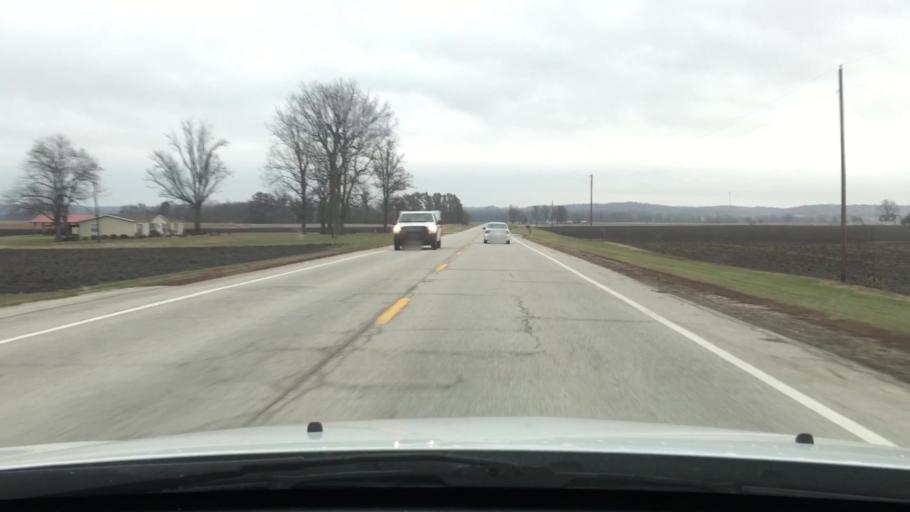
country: US
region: Missouri
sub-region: Pike County
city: Louisiana
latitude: 39.4889
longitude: -91.0101
